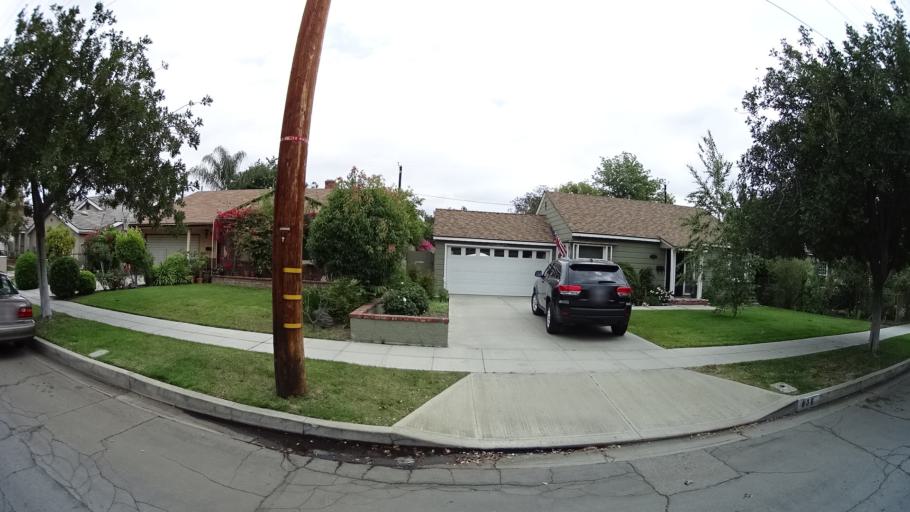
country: US
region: California
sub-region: Los Angeles County
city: Universal City
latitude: 34.1630
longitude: -118.3538
